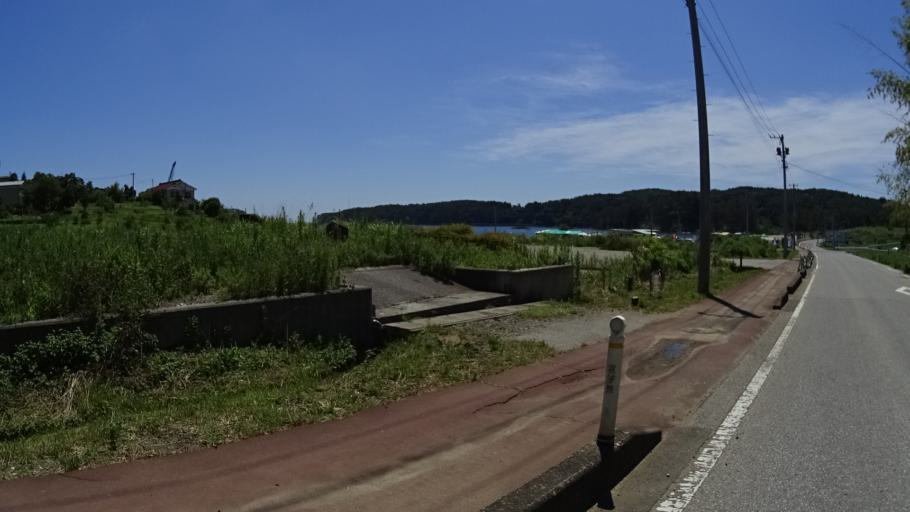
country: JP
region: Iwate
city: Ofunato
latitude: 38.8548
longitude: 141.6214
